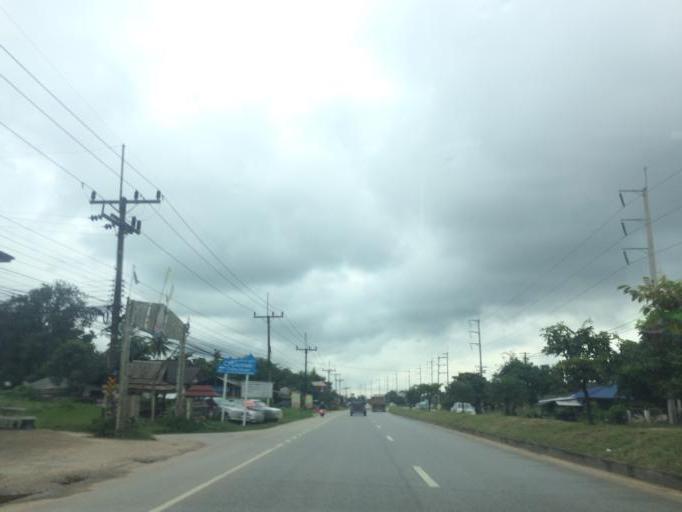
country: TH
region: Chiang Rai
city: Mae Chan
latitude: 20.0720
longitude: 99.8755
